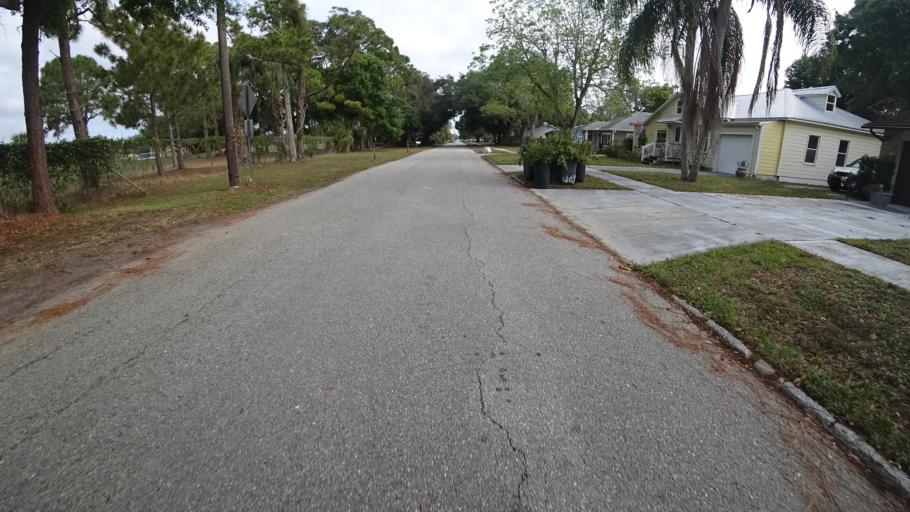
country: US
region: Florida
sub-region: Manatee County
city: West Bradenton
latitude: 27.4893
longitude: -82.6060
